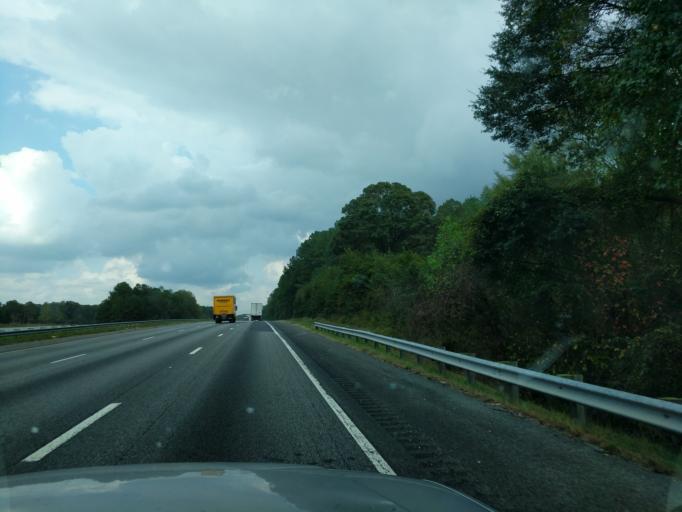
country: US
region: South Carolina
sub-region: Anderson County
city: Northlake
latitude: 34.5914
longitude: -82.6697
